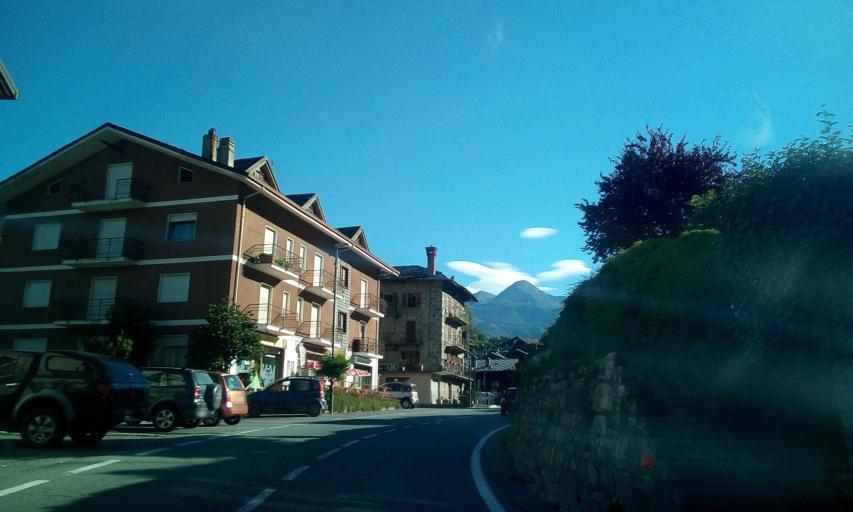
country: IT
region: Aosta Valley
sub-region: Valle d'Aosta
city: Challand-Saint-Anselme
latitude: 45.7059
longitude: 7.7327
